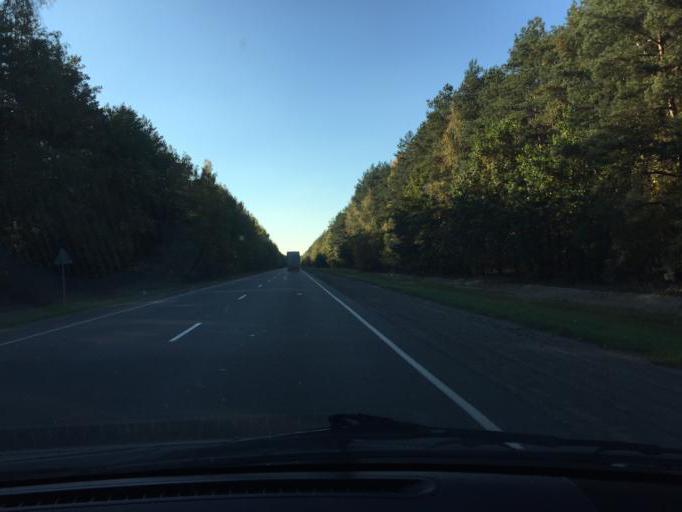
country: BY
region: Brest
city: Luninyets
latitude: 52.2765
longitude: 26.8633
